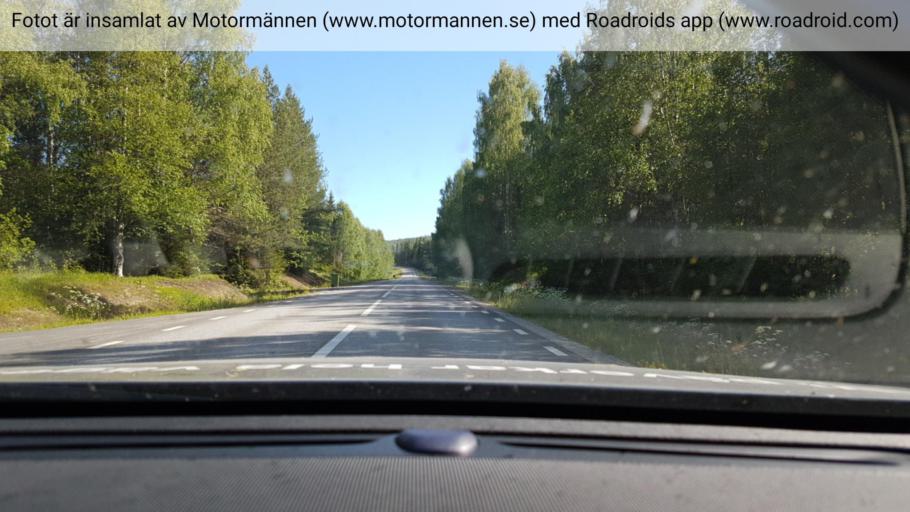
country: SE
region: Vaesterbotten
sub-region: Lycksele Kommun
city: Lycksele
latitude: 64.6626
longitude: 18.4477
